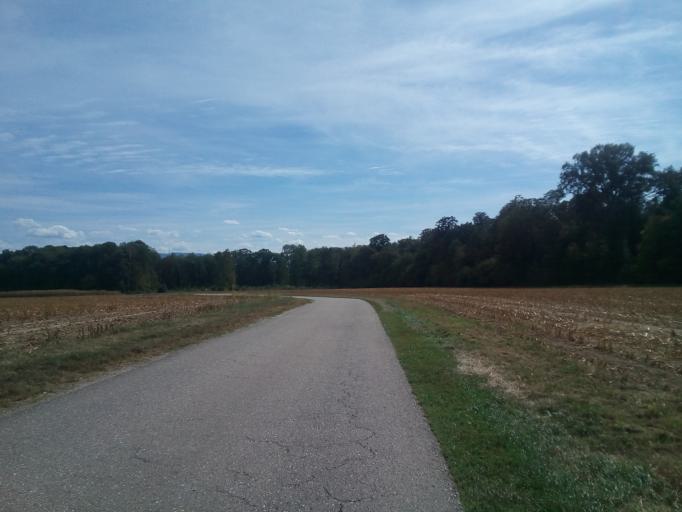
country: DE
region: Baden-Wuerttemberg
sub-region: Karlsruhe Region
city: Lichtenau
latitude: 48.7042
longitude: 8.0140
